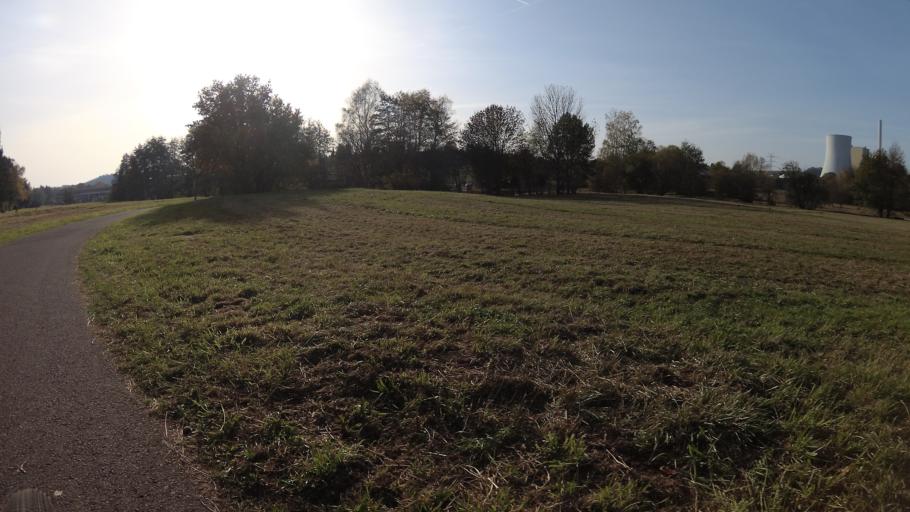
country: DE
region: Saarland
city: Bexbach
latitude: 49.3587
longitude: 7.2580
